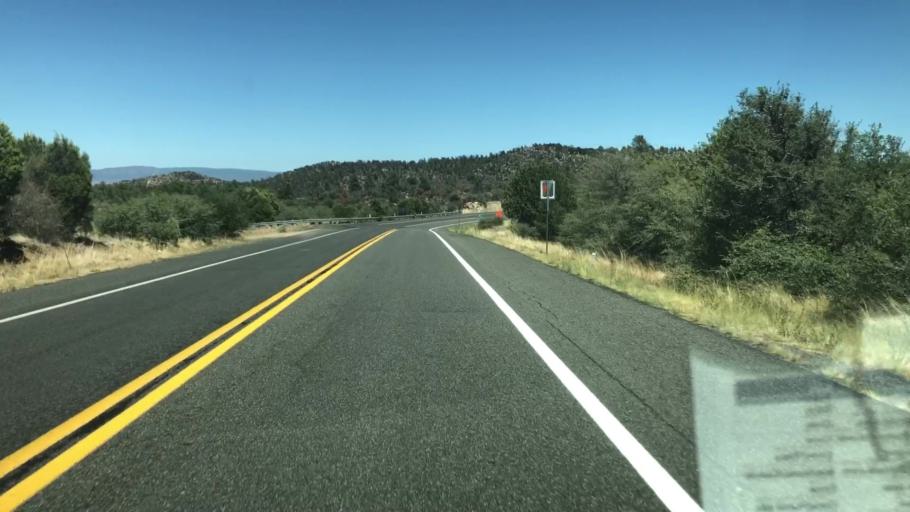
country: US
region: Arizona
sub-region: Yavapai County
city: Prescott
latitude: 34.5783
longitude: -112.5254
